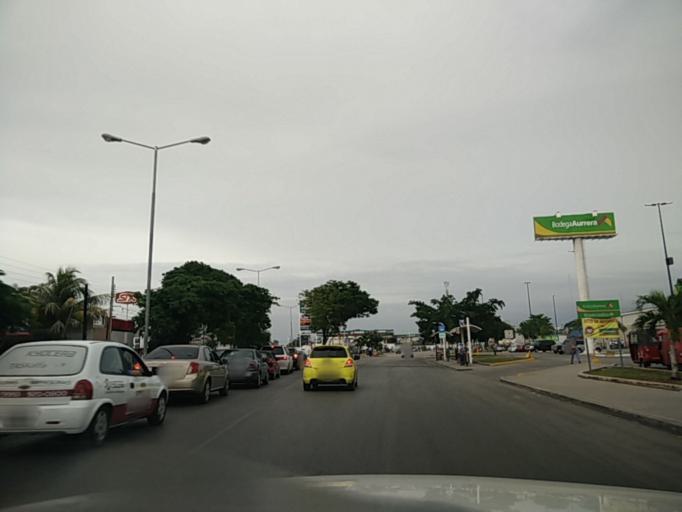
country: MX
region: Yucatan
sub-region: Kanasin
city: Kanasin
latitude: 20.9600
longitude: -89.5793
